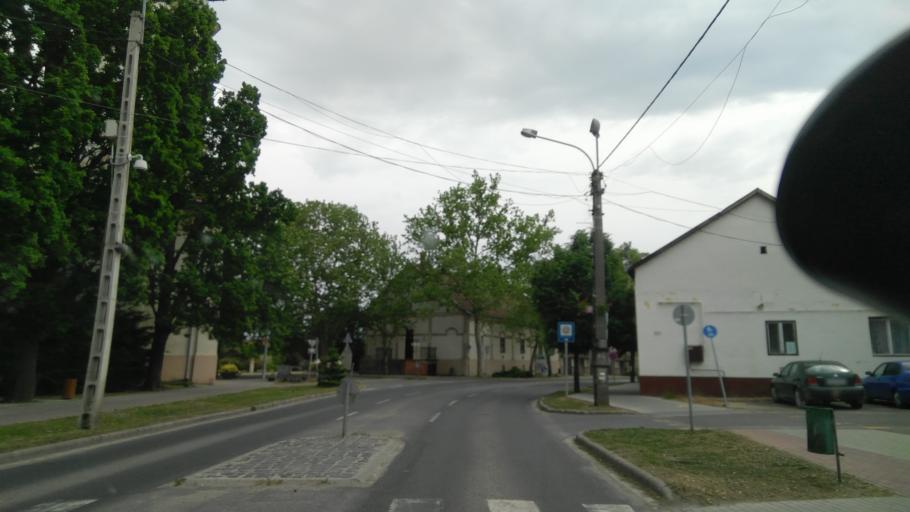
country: HU
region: Bekes
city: Sarkad
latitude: 46.7441
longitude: 21.3832
